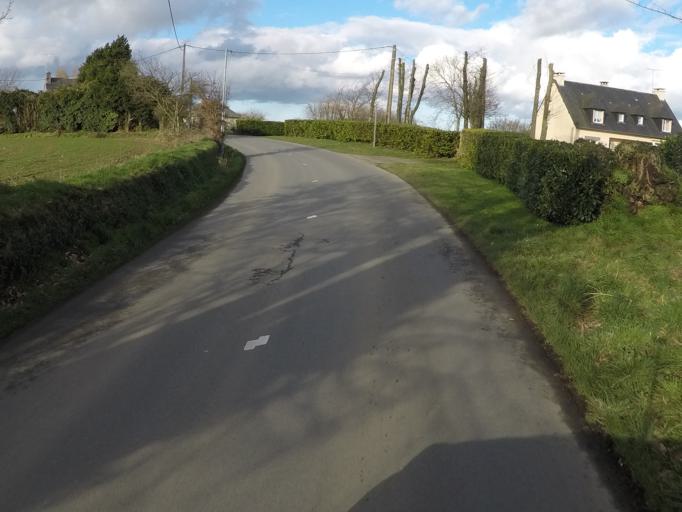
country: FR
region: Brittany
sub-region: Departement des Cotes-d'Armor
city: Plouagat
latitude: 48.5491
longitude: -2.9809
